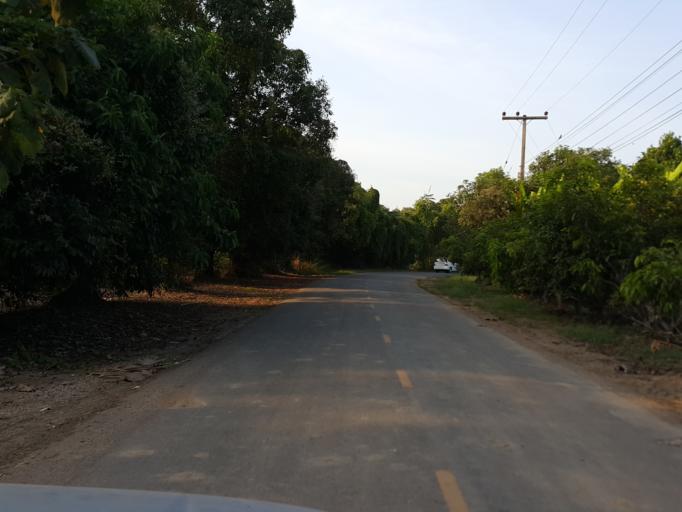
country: TH
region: Sukhothai
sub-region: Amphoe Si Satchanalai
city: Si Satchanalai
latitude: 17.4284
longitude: 99.7915
